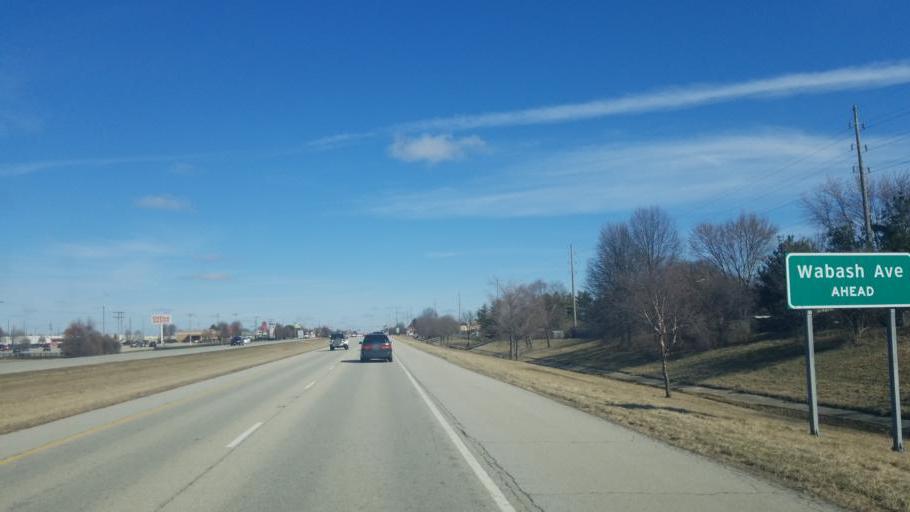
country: US
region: Illinois
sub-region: Sangamon County
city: Jerome
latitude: 39.7598
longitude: -89.7062
